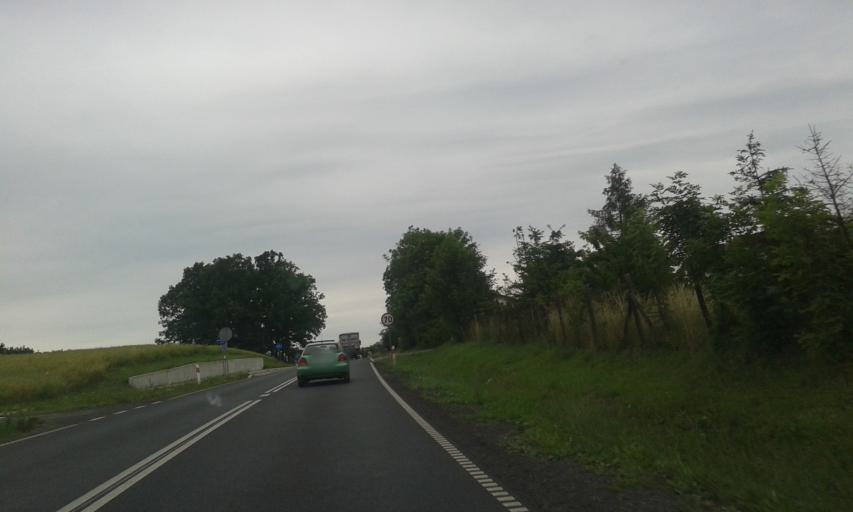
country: PL
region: Kujawsko-Pomorskie
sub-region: Powiat bydgoski
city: Koronowo
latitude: 53.2082
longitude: 17.9254
